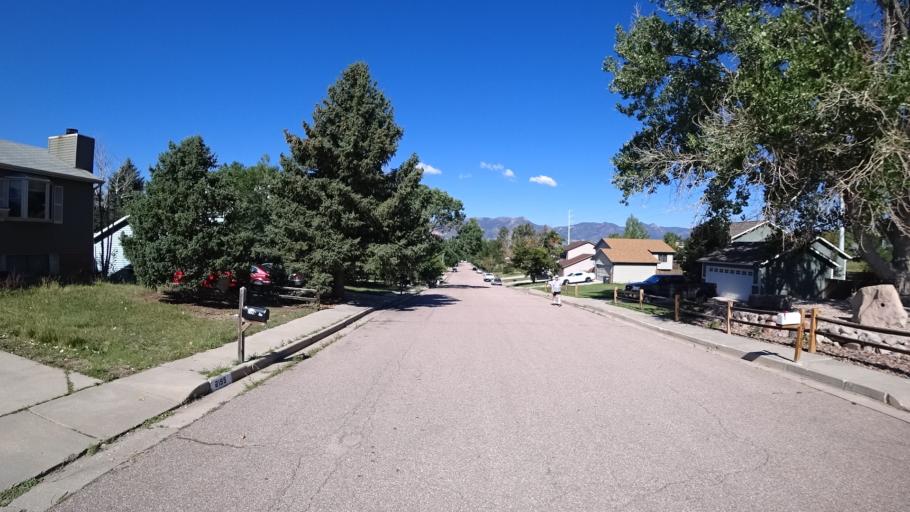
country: US
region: Colorado
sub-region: El Paso County
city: Air Force Academy
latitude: 38.9435
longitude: -104.7852
